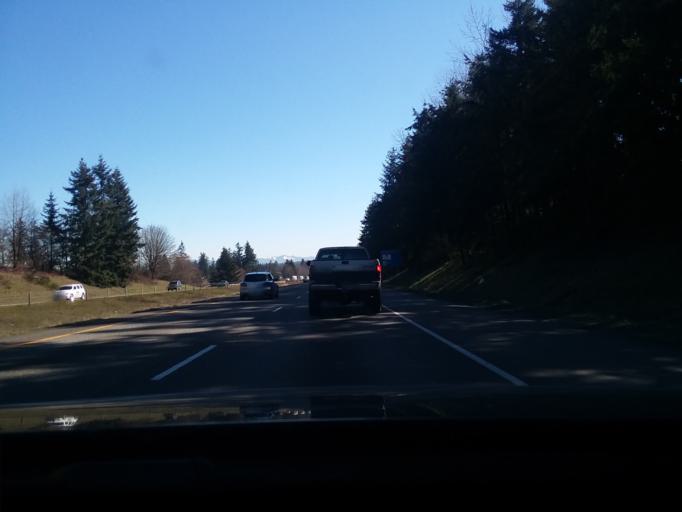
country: US
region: Washington
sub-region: Pierce County
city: Summit
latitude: 47.1580
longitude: -122.3315
